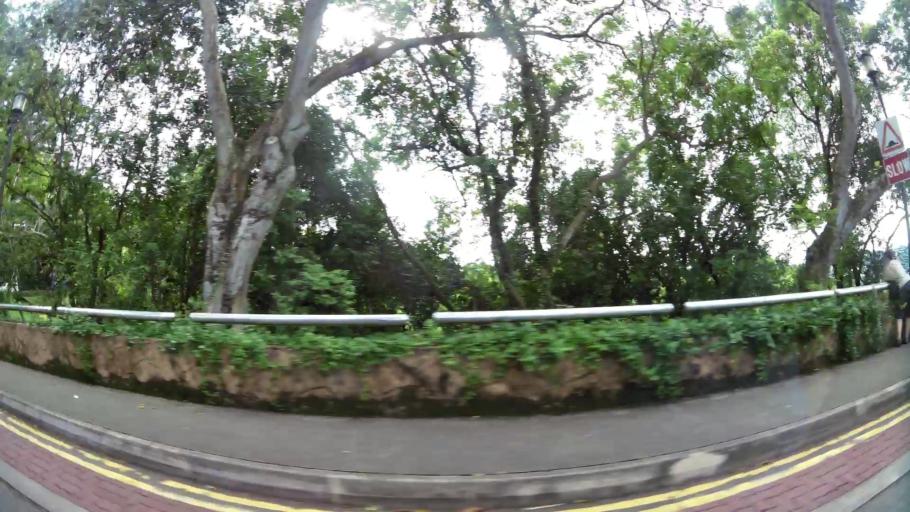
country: SG
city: Singapore
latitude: 1.2727
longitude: 103.8174
